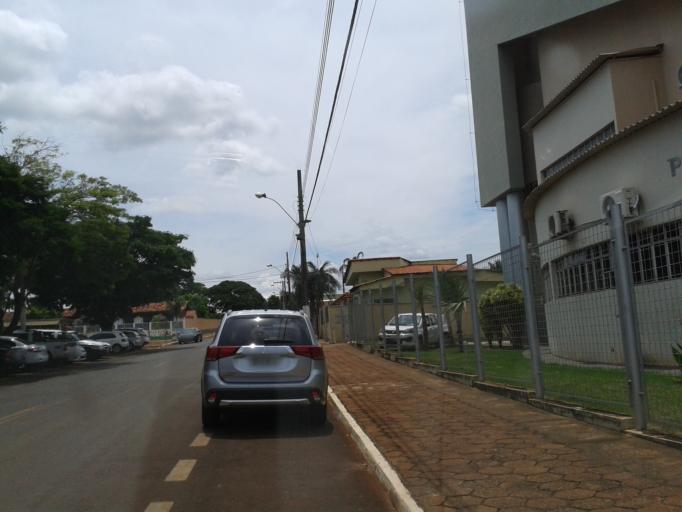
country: BR
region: Minas Gerais
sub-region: Centralina
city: Centralina
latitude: -18.7233
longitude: -49.2023
